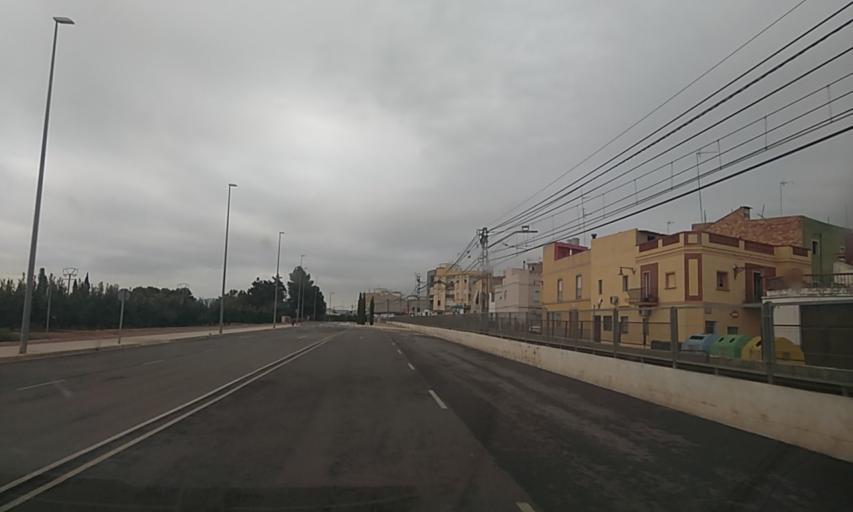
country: ES
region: Valencia
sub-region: Provincia de Valencia
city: L'Alcudia
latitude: 39.1976
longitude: -0.5098
